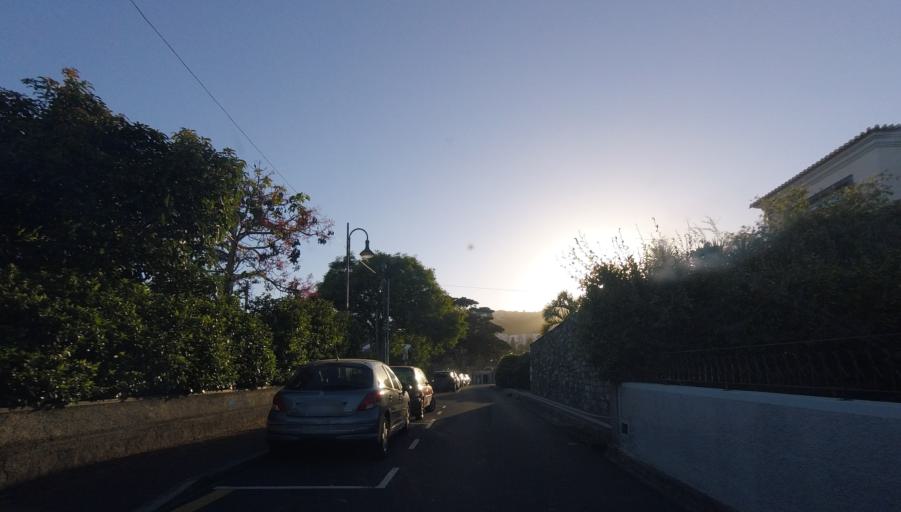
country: PT
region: Madeira
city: Canico
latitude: 32.6430
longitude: -16.8350
